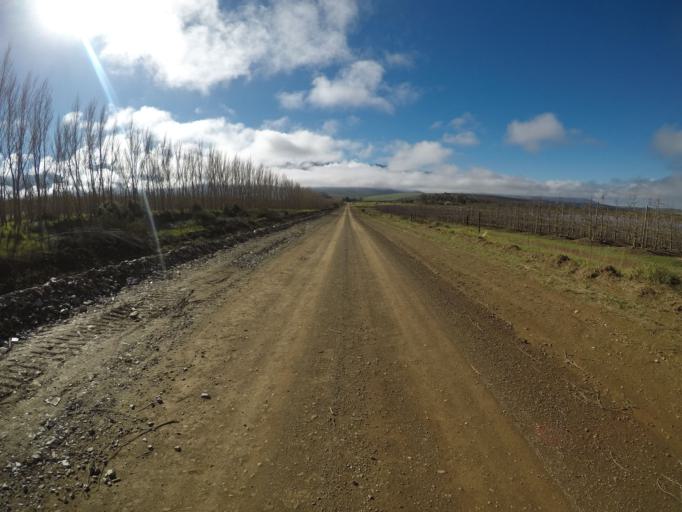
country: ZA
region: Western Cape
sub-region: Overberg District Municipality
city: Caledon
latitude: -34.1171
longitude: 19.7387
